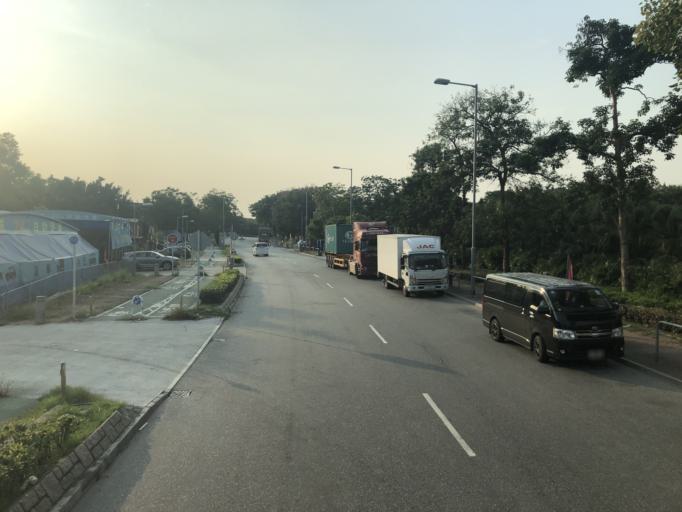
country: HK
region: Yuen Long
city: Yuen Long Kau Hui
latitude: 22.4549
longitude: 113.9936
